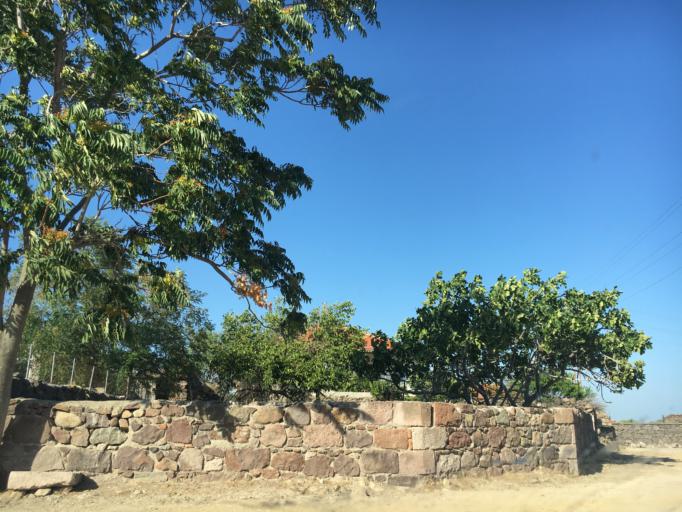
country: TR
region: Canakkale
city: Behram
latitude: 39.5029
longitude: 26.2557
